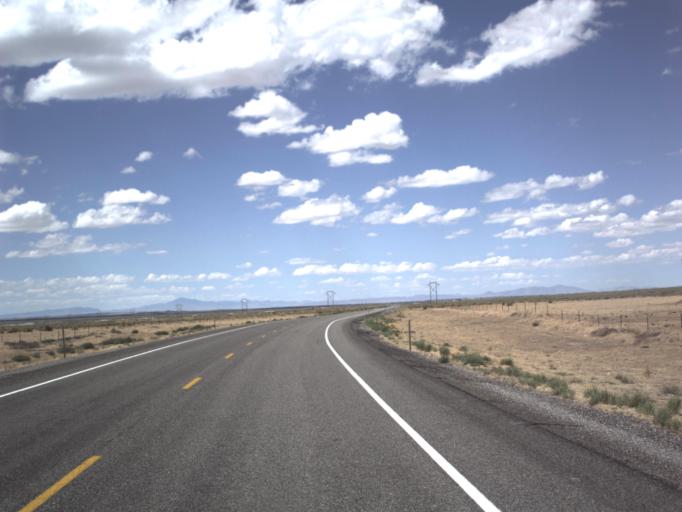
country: US
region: Utah
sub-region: Millard County
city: Fillmore
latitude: 39.1499
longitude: -112.3957
